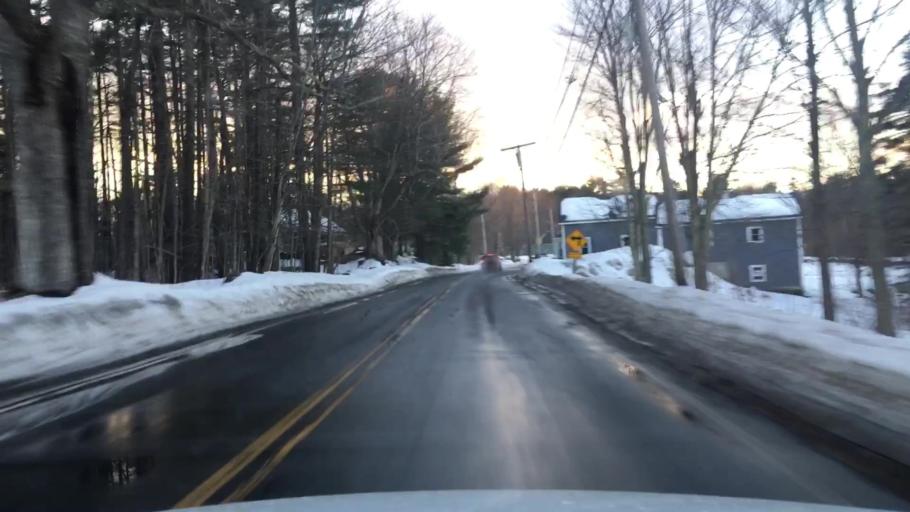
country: US
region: Maine
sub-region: York County
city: Newfield
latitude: 43.6428
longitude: -70.9216
